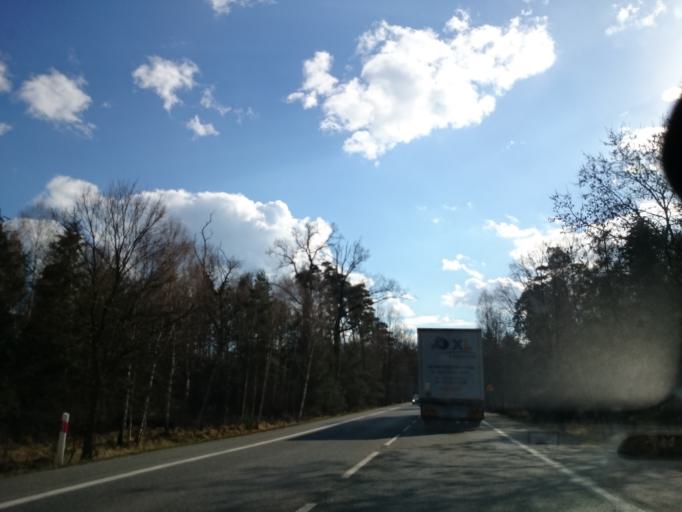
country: PL
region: Opole Voivodeship
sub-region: Powiat opolski
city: Dabrowa
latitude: 50.6705
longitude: 17.7044
